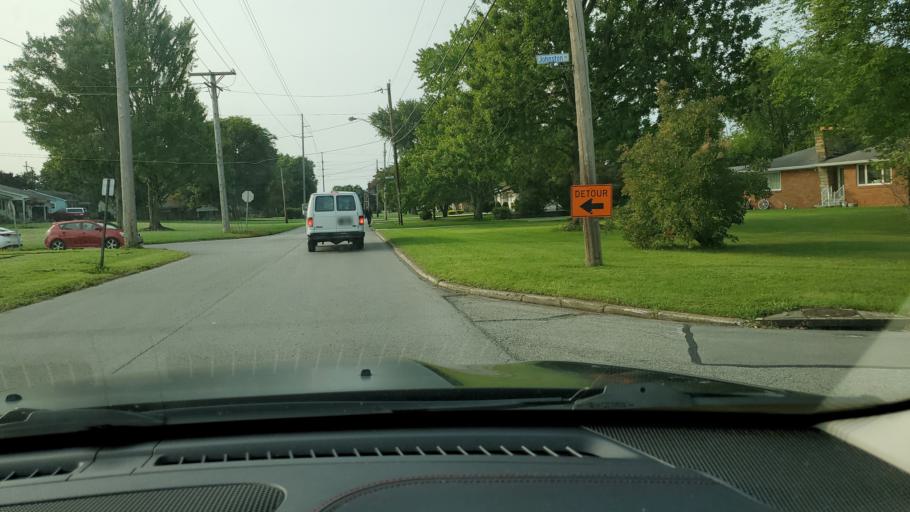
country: US
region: Ohio
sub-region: Mahoning County
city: Poland
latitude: 41.0338
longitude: -80.6212
